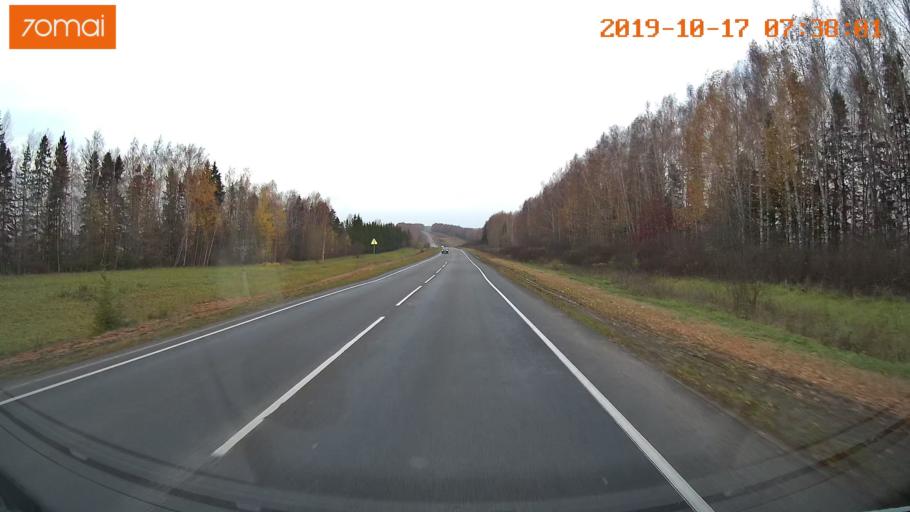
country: RU
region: Vladimir
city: Yur'yev-Pol'skiy
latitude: 56.4524
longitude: 39.8848
